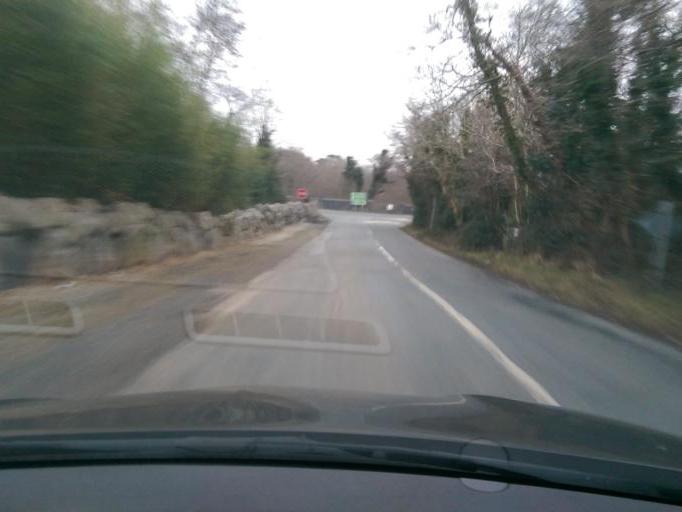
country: IE
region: Connaught
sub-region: County Galway
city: Moycullen
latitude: 53.3130
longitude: -9.1483
